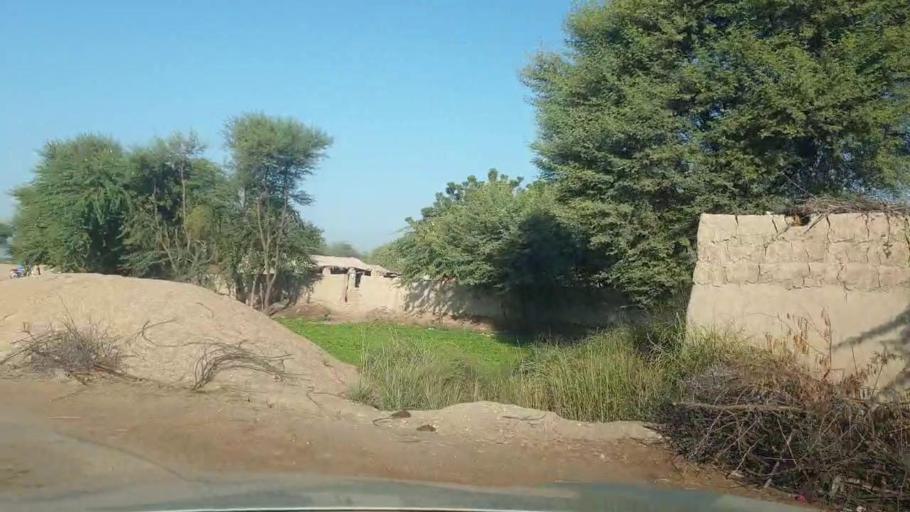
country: PK
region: Sindh
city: Bhan
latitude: 26.5548
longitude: 67.6868
